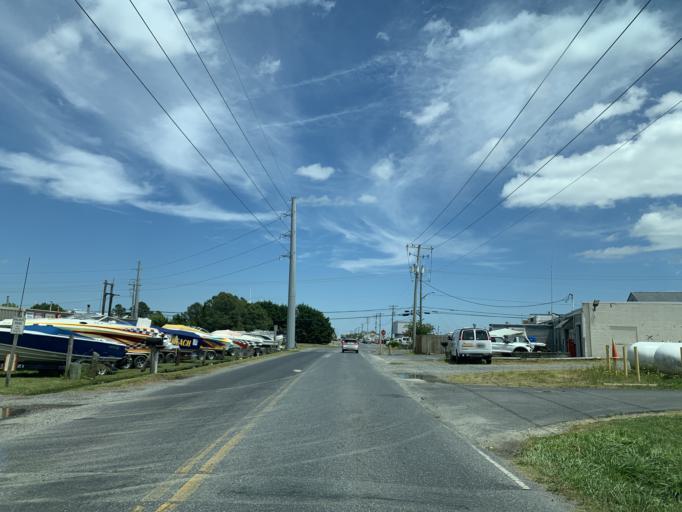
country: US
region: Maryland
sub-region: Worcester County
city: West Ocean City
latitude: 38.3279
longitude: -75.1088
